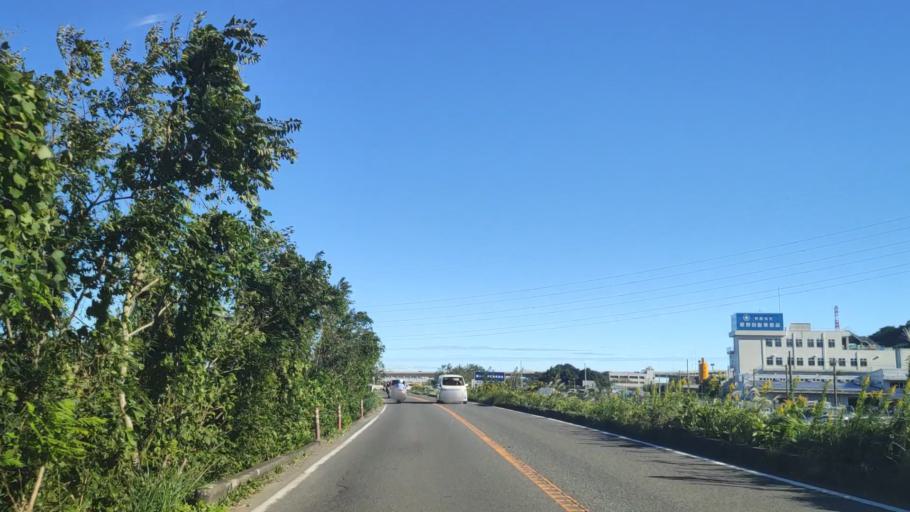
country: JP
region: Kanagawa
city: Zama
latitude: 35.5287
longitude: 139.3492
